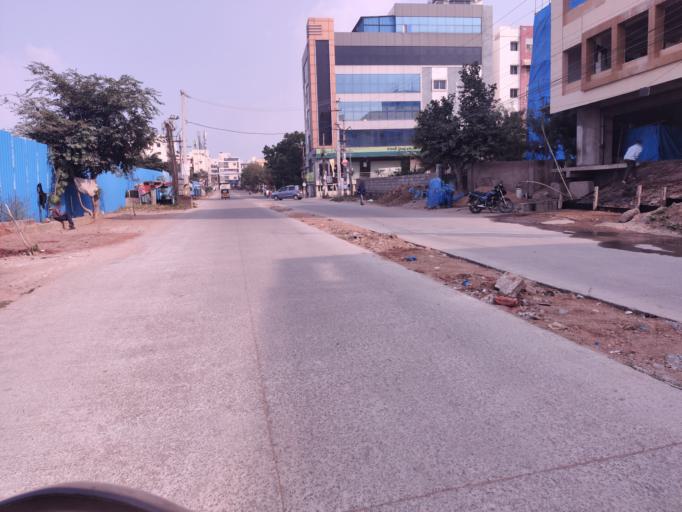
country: IN
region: Telangana
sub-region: Hyderabad
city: Hyderabad
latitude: 17.4034
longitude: 78.3886
